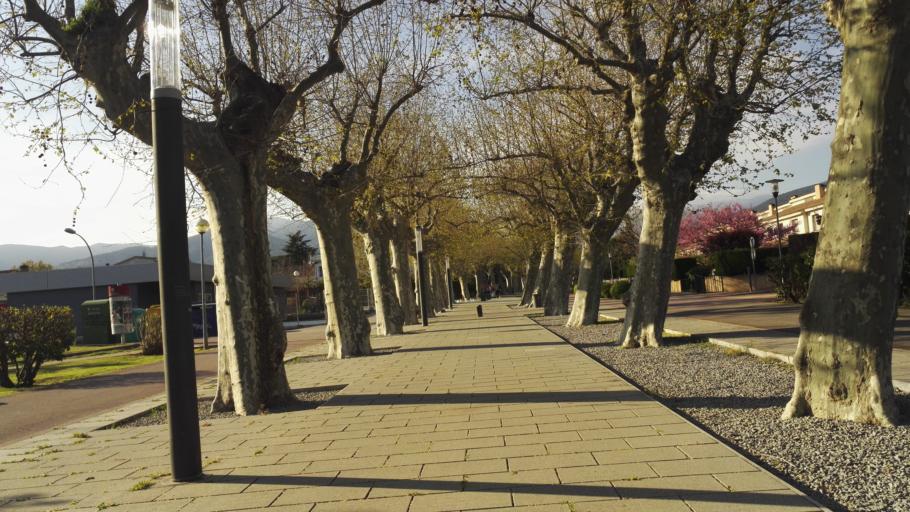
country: ES
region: Catalonia
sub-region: Provincia de Barcelona
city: Santa Maria de Palautordera
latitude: 41.6969
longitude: 2.4404
